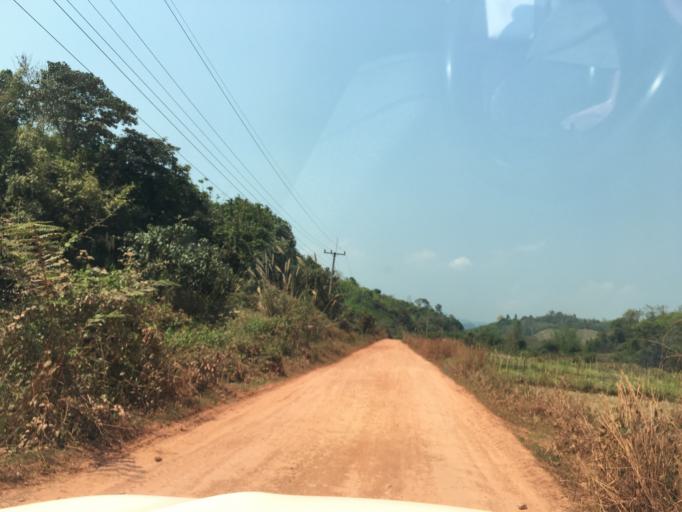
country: LA
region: Bolikhamxai
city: Bolikhan
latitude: 18.7455
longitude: 103.6174
